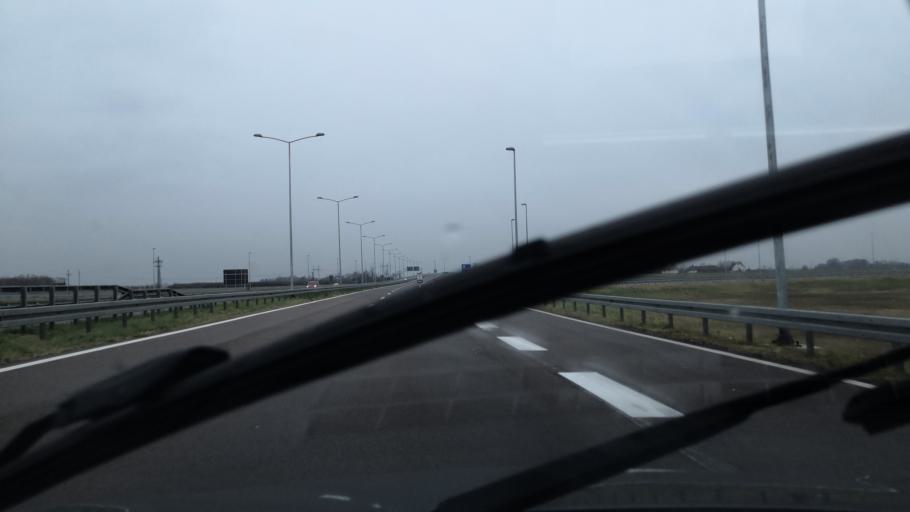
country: RS
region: Autonomna Pokrajina Vojvodina
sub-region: Severnobacki Okrug
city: Subotica
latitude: 46.0305
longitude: 19.7379
